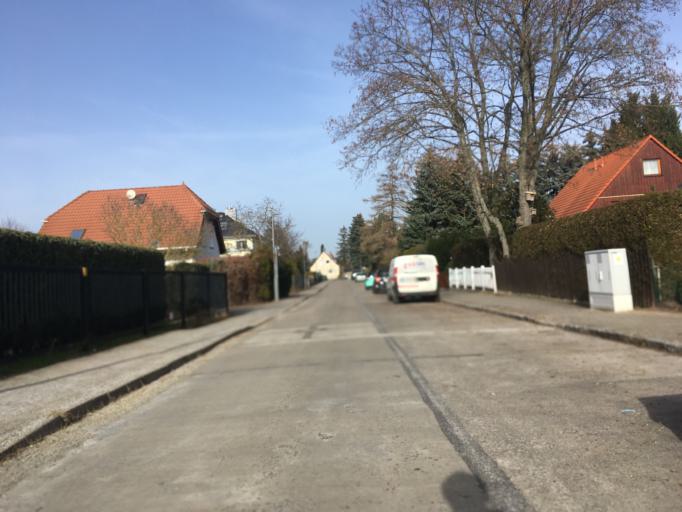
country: DE
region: Berlin
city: Bohnsdorf
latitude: 52.3969
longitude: 13.5686
